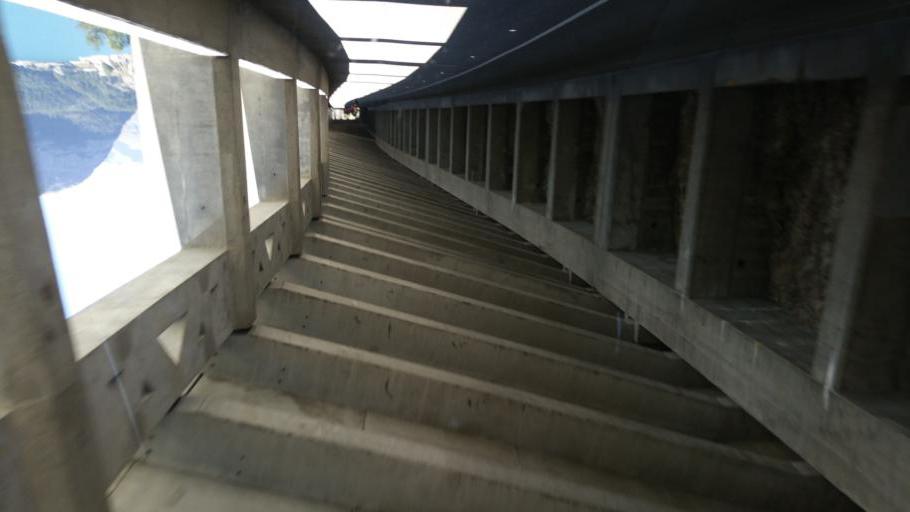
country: FR
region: Rhone-Alpes
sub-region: Departement de la Savoie
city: Tignes
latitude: 45.4951
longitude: 6.9352
